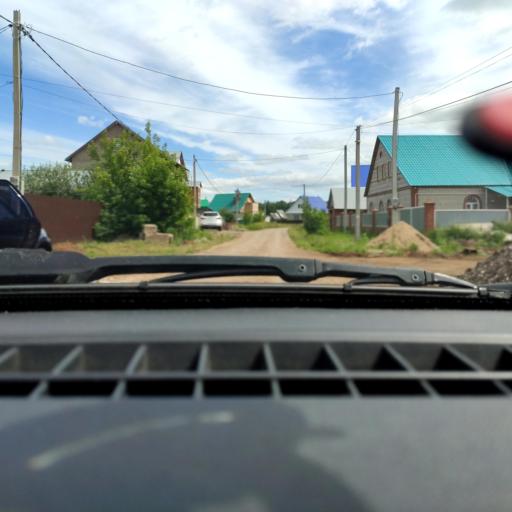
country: RU
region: Bashkortostan
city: Iglino
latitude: 54.7902
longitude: 56.2488
